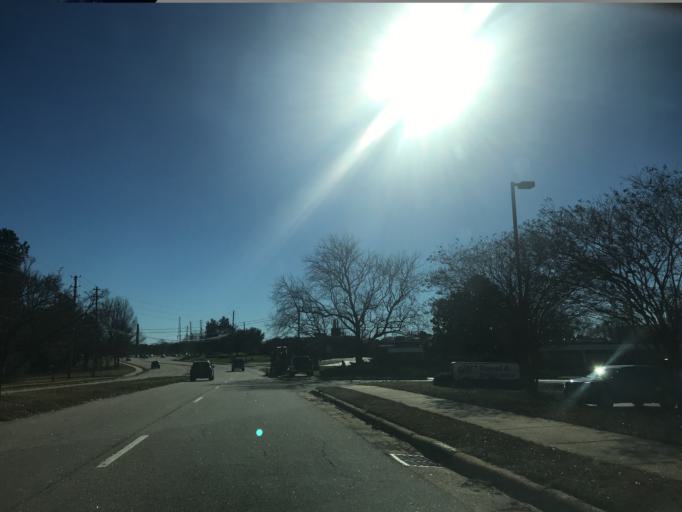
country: US
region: North Carolina
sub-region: Wake County
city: West Raleigh
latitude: 35.8126
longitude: -78.7058
